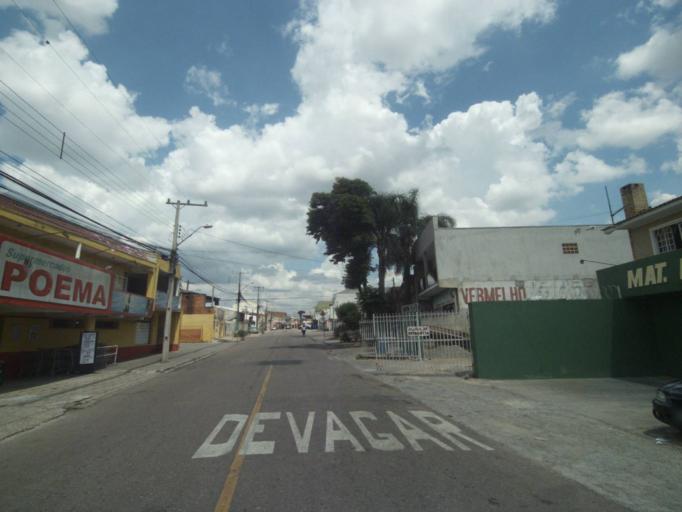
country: BR
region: Parana
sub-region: Sao Jose Dos Pinhais
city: Sao Jose dos Pinhais
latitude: -25.5315
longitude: -49.2756
